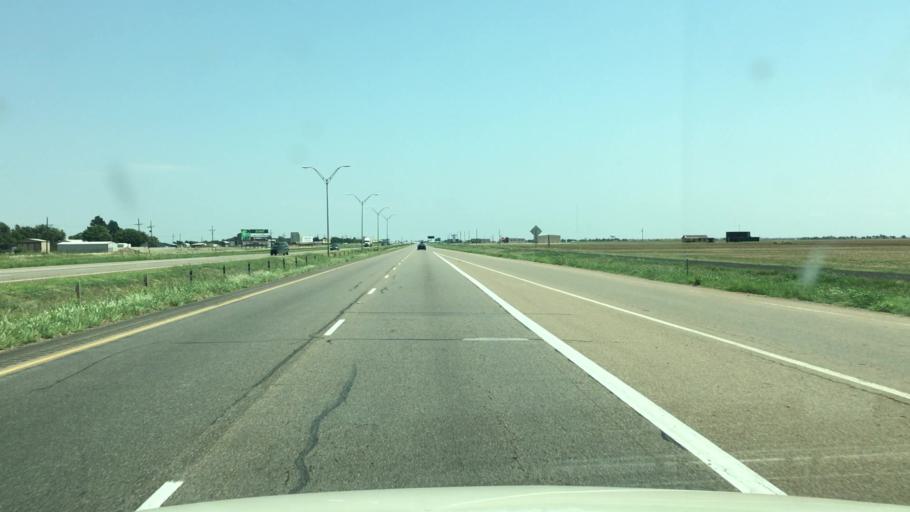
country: US
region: Texas
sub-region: Potter County
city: Bushland
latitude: 35.1898
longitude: -102.0053
